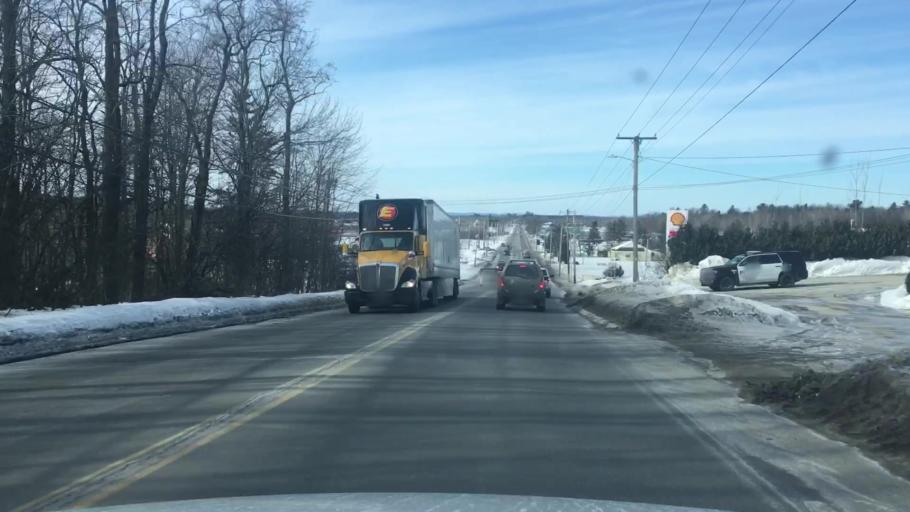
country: US
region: Maine
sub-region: Penobscot County
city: Bangor
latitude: 44.8338
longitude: -68.7891
